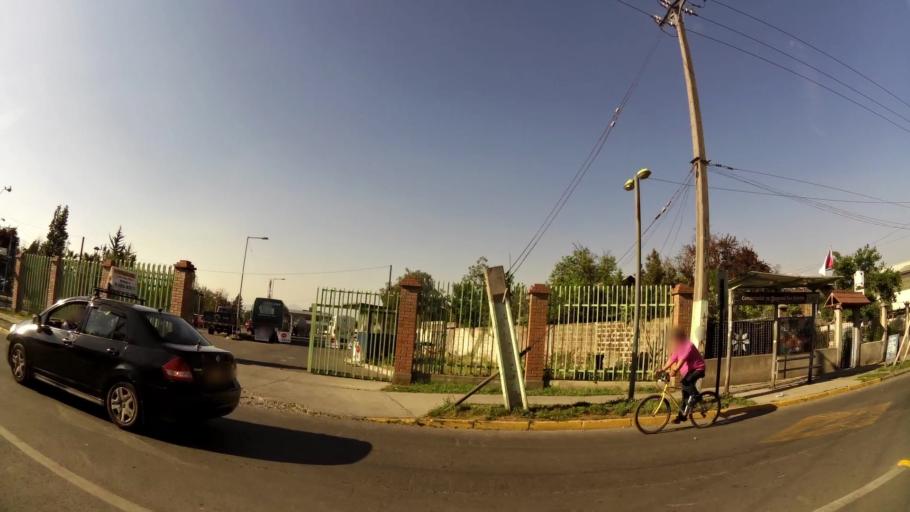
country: CL
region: Santiago Metropolitan
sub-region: Provincia de Santiago
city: La Pintana
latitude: -33.5451
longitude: -70.6308
